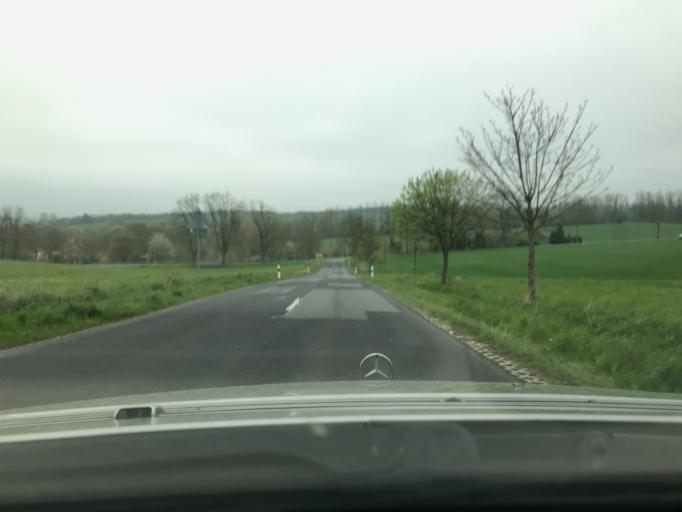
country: DE
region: Thuringia
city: Kreuzebra
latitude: 51.3377
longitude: 10.2622
